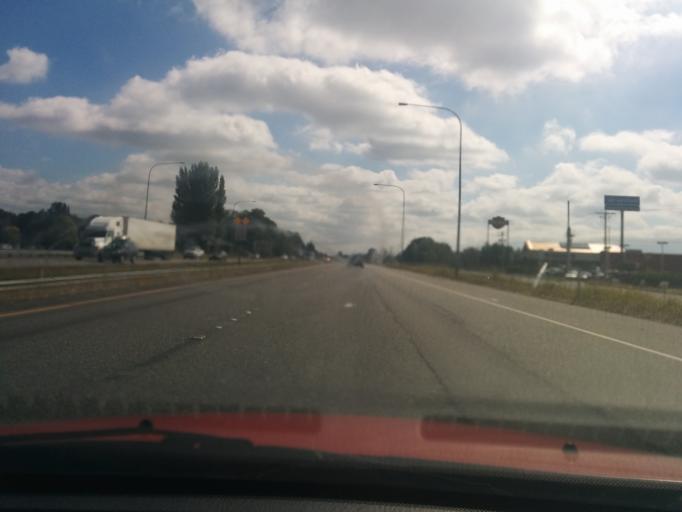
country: US
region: Washington
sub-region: Skagit County
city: Burlington
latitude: 48.4618
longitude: -122.3417
